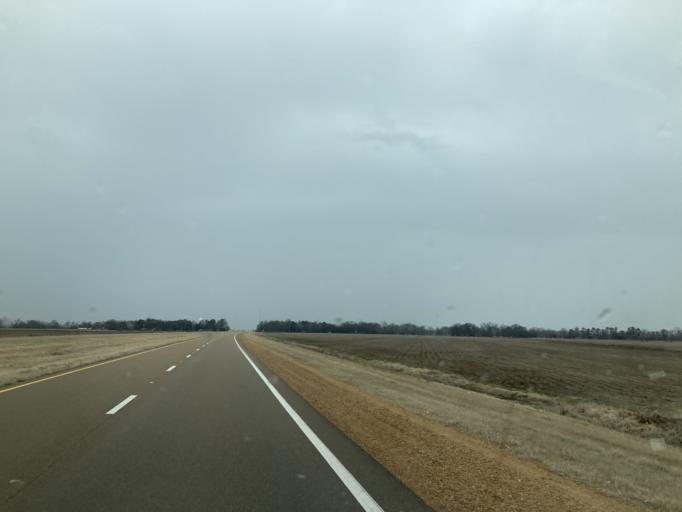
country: US
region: Mississippi
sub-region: Humphreys County
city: Belzoni
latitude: 33.0843
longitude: -90.4853
